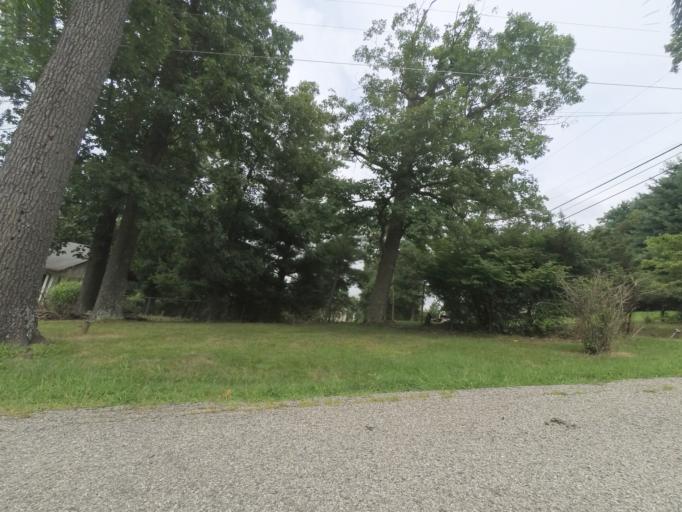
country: US
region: West Virginia
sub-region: Cabell County
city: Huntington
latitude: 38.3980
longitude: -82.4374
